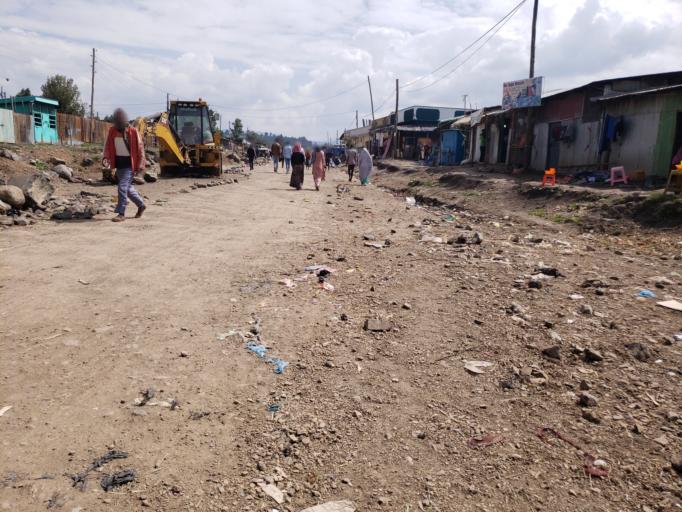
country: ET
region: Oromiya
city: Dodola
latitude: 7.0071
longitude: 39.3916
